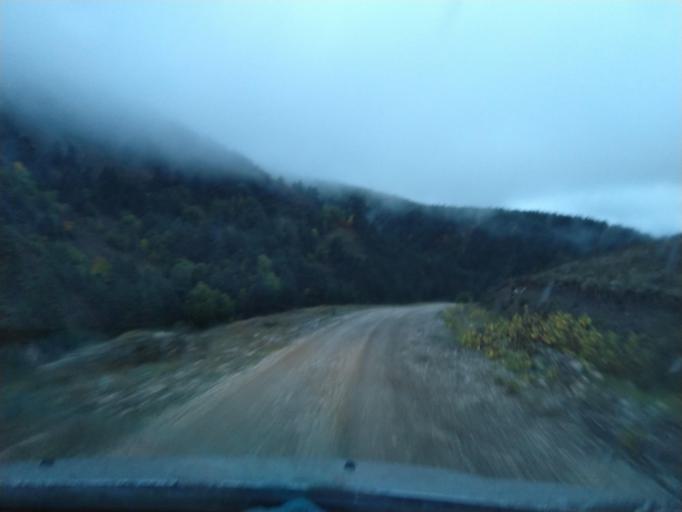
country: RU
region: North Ossetia
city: Tarskoye
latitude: 42.8258
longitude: 44.9760
